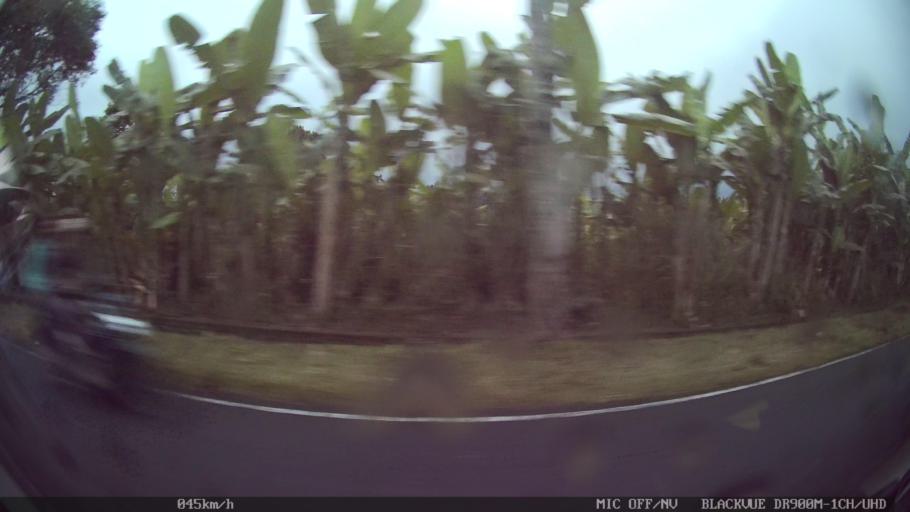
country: ID
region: Bali
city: Banjar Ponggang
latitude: -8.3945
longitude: 115.2548
